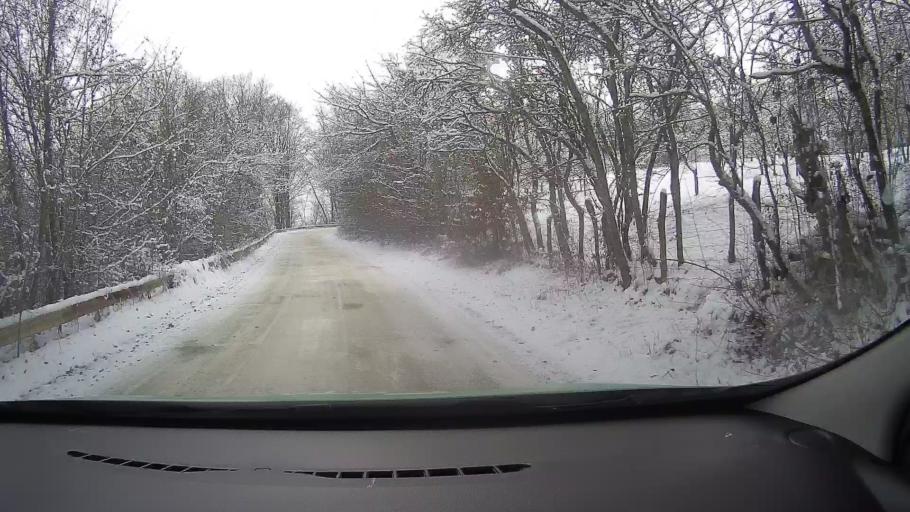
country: RO
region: Alba
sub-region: Comuna Almasu Mare
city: Almasu Mare
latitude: 46.0944
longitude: 23.1680
